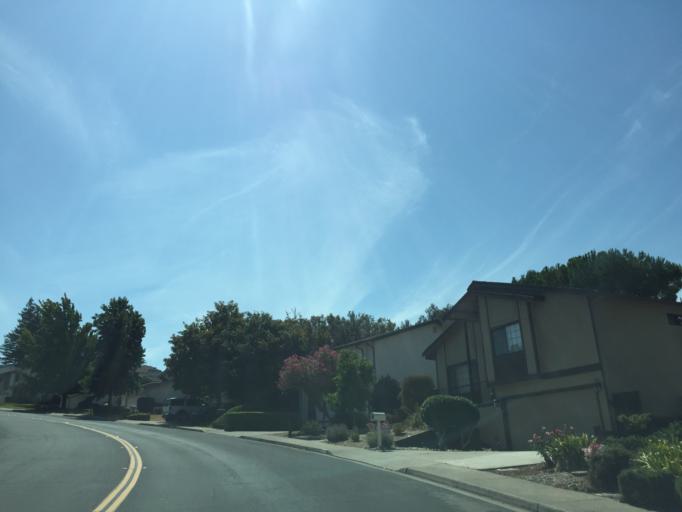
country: US
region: California
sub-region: Contra Costa County
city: Mountain View
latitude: 38.0040
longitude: -122.1243
